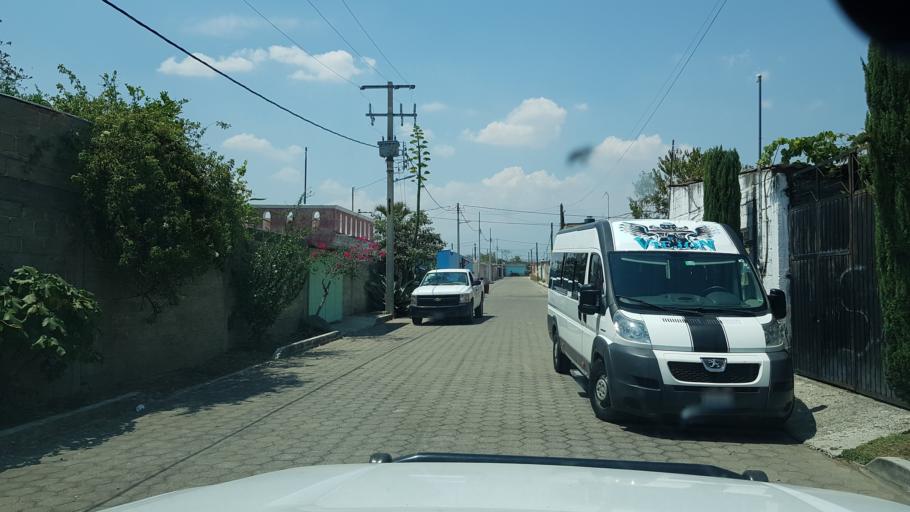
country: MX
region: Puebla
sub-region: Huaquechula
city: Cacaloxuchitl
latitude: 18.7913
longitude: -98.4677
